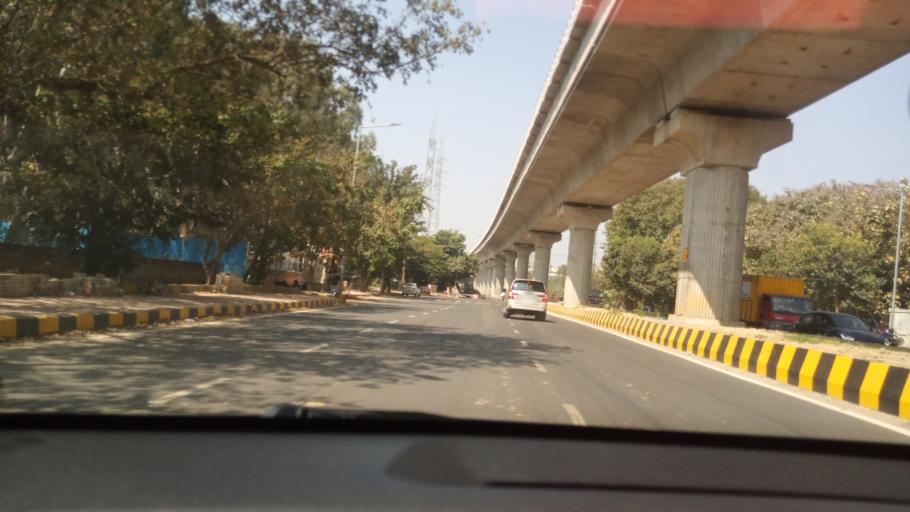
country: IN
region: Karnataka
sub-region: Bangalore Rural
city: Hoskote
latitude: 12.9771
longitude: 77.7199
